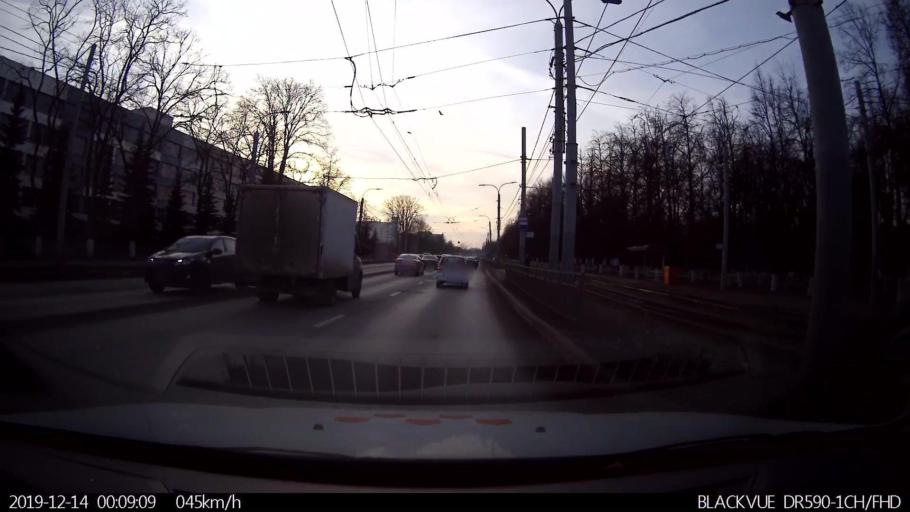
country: RU
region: Nizjnij Novgorod
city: Gorbatovka
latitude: 56.2462
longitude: 43.8746
